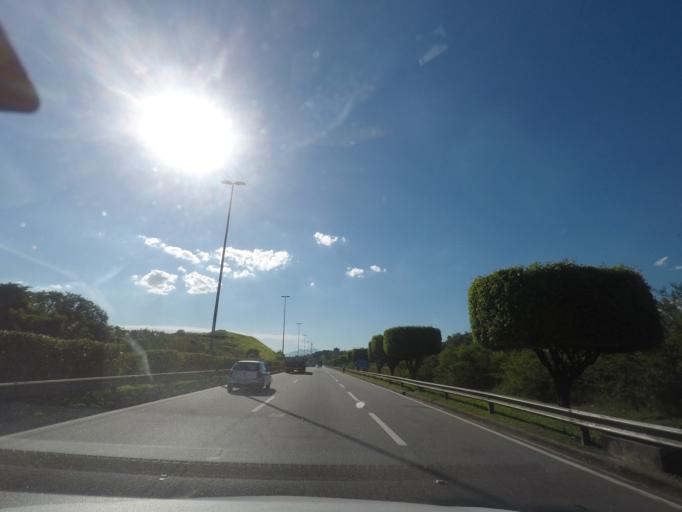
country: BR
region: Rio de Janeiro
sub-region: Petropolis
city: Petropolis
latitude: -22.6480
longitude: -43.1809
